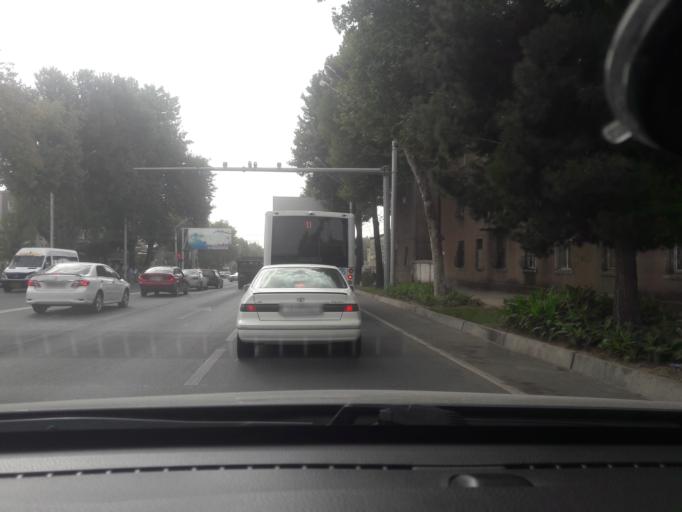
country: TJ
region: Dushanbe
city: Dushanbe
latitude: 38.5760
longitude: 68.8042
